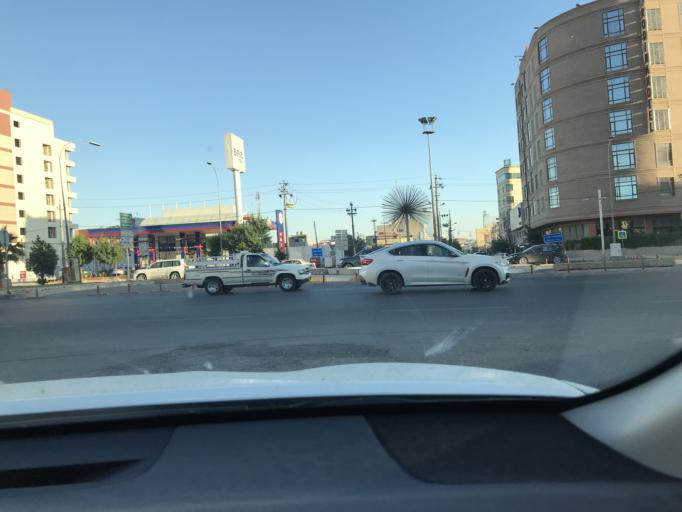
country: IQ
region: Arbil
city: Erbil
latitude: 36.2040
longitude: 44.0099
